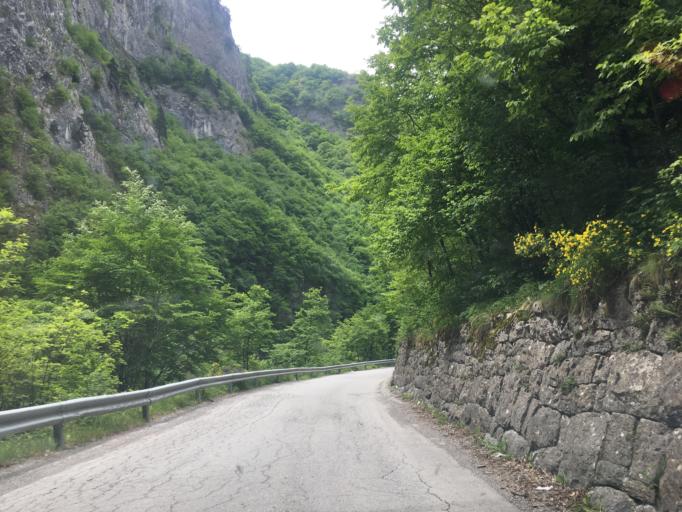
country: XK
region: Pec
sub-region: Komuna e Pejes
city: Peje
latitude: 42.6633
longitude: 20.2199
